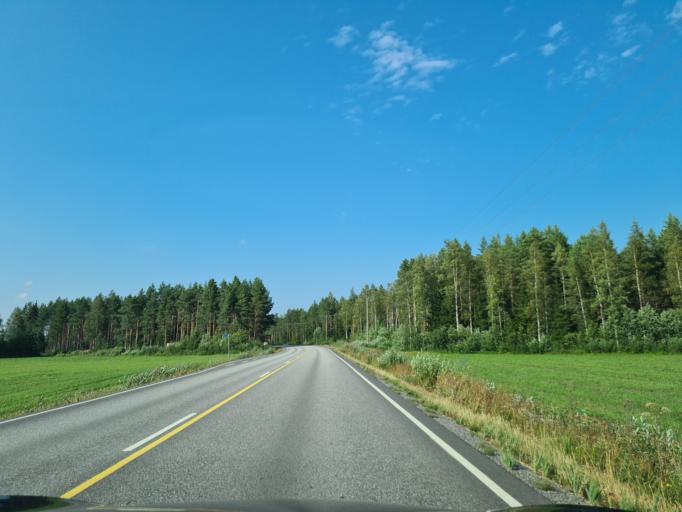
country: FI
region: Satakunta
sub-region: Pohjois-Satakunta
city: Kankaanpaeae
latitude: 61.9207
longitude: 22.5069
